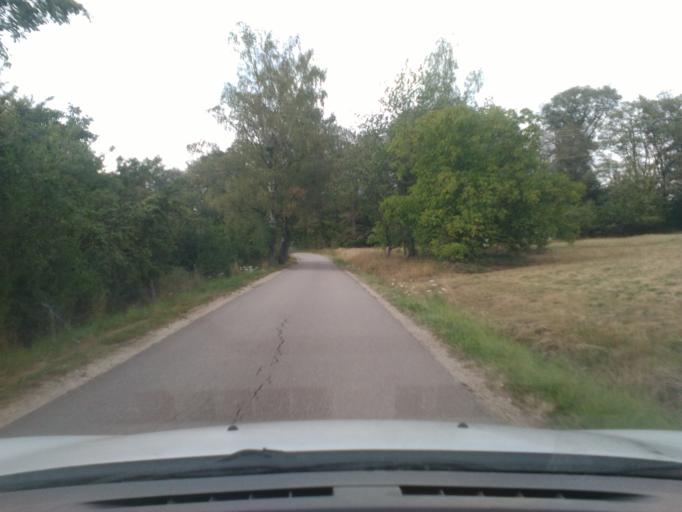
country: FR
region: Lorraine
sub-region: Departement des Vosges
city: Portieux
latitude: 48.3352
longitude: 6.3587
